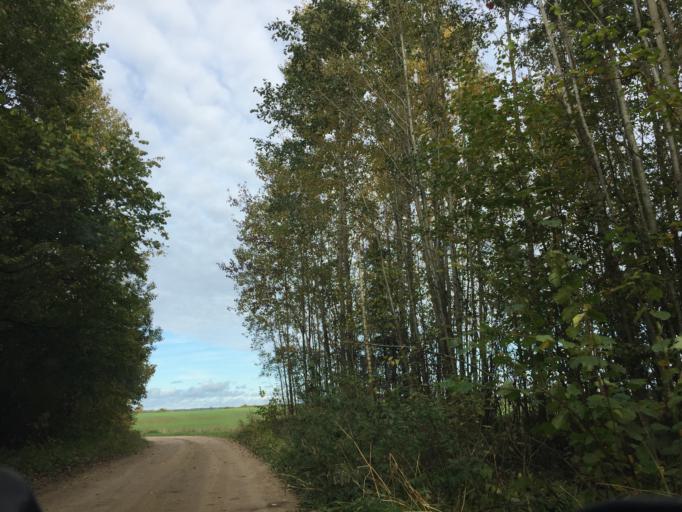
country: LV
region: Jaunpils
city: Jaunpils
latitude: 56.6464
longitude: 23.0798
